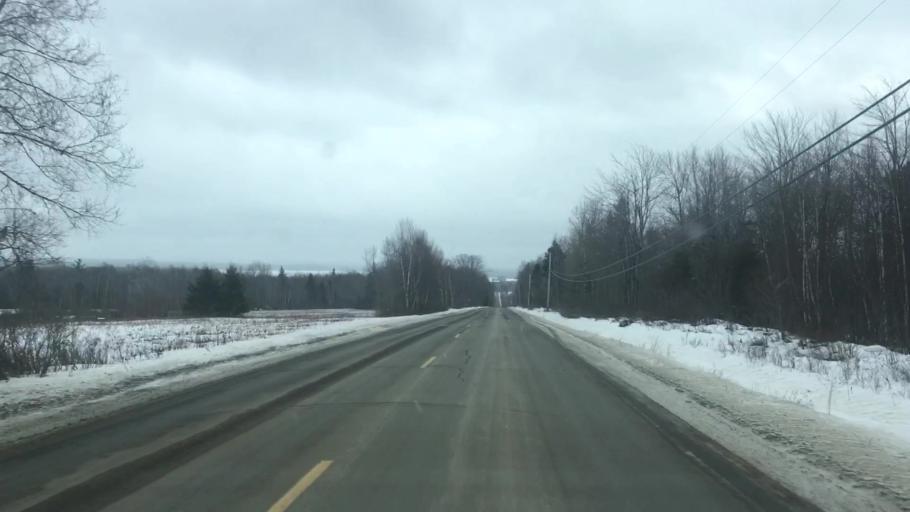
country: US
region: Maine
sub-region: Washington County
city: East Machias
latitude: 44.9790
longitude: -67.4529
